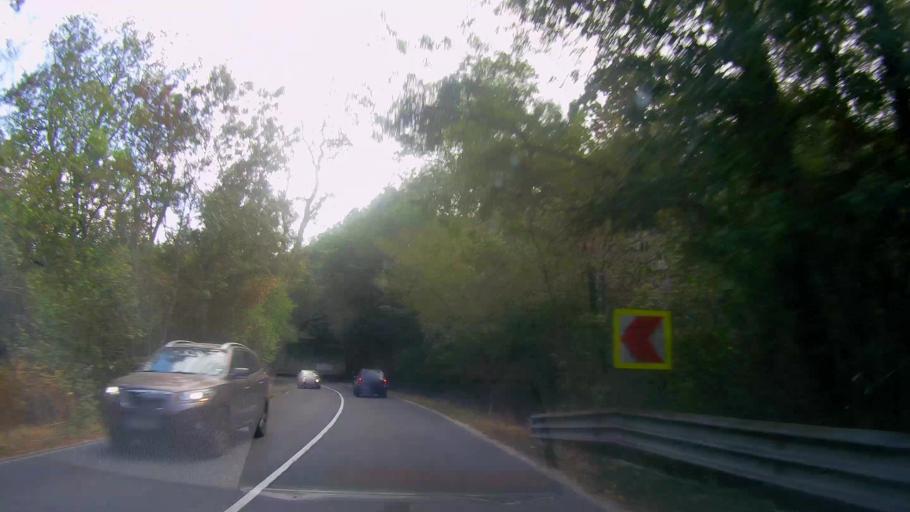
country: BG
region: Burgas
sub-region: Obshtina Primorsko
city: Primorsko
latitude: 42.3047
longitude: 27.7224
